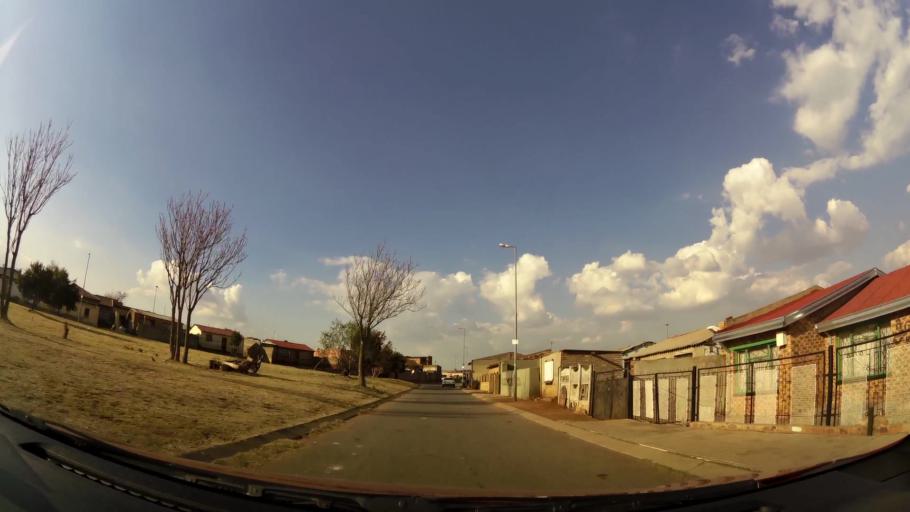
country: ZA
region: Gauteng
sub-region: City of Johannesburg Metropolitan Municipality
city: Soweto
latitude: -26.2350
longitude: 27.8622
